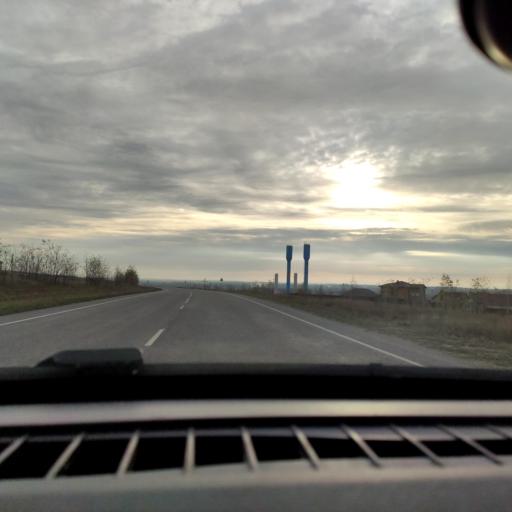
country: RU
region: Belgorod
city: Ilovka
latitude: 50.6473
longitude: 38.6297
